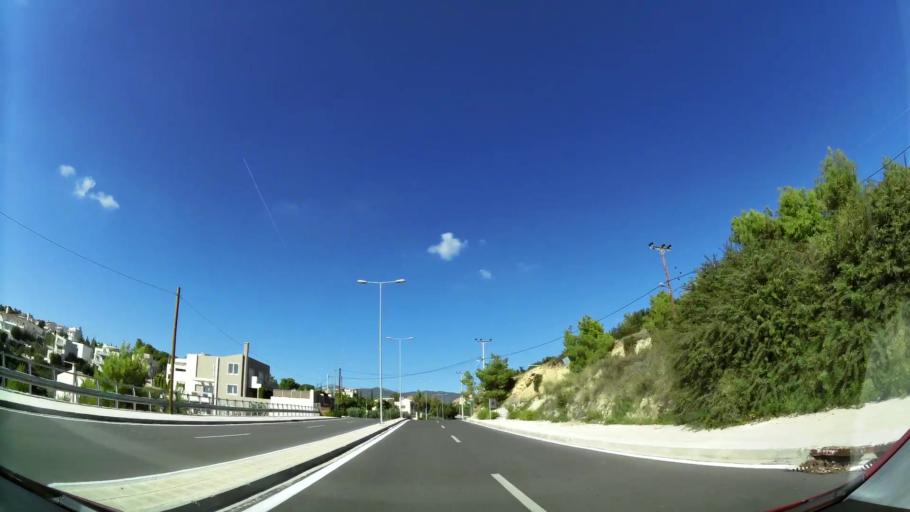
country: GR
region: Attica
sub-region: Nomarchia Anatolikis Attikis
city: Dhrafi
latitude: 38.0116
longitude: 23.9118
